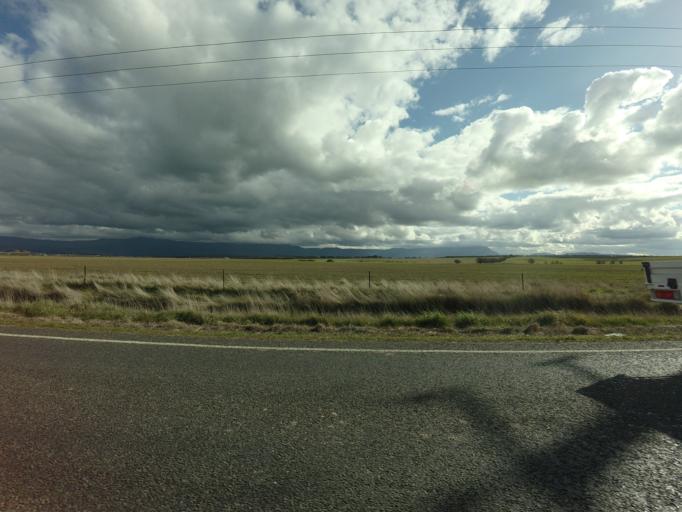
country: AU
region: Tasmania
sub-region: Northern Midlands
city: Longford
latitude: -41.7065
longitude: 147.0790
